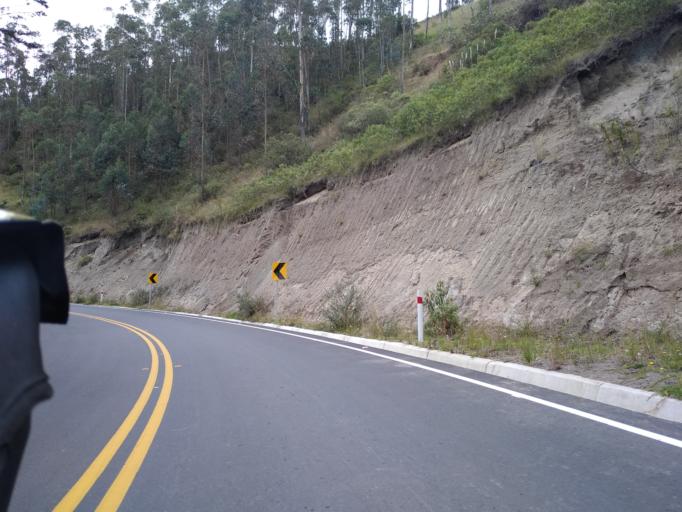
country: EC
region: Cotopaxi
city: Saquisili
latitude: -0.7780
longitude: -78.9103
